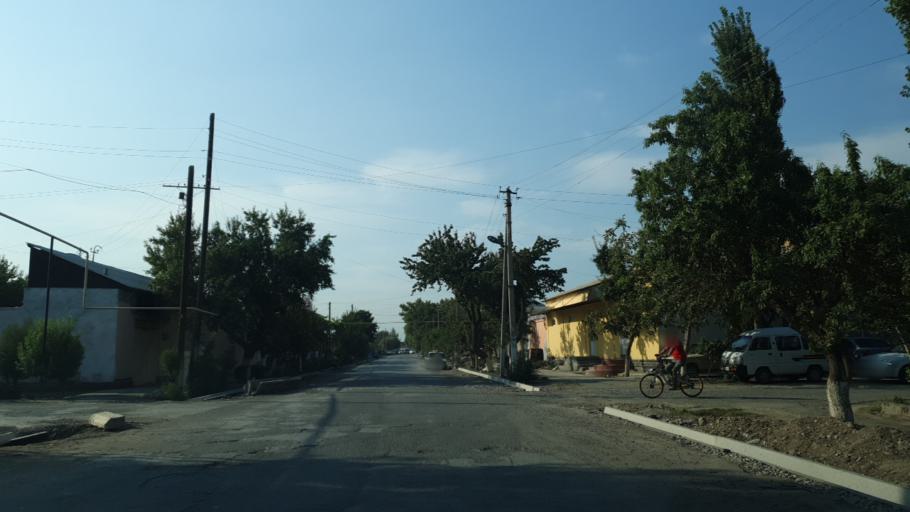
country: UZ
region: Fergana
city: Yaypan
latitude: 40.3763
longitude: 70.8120
